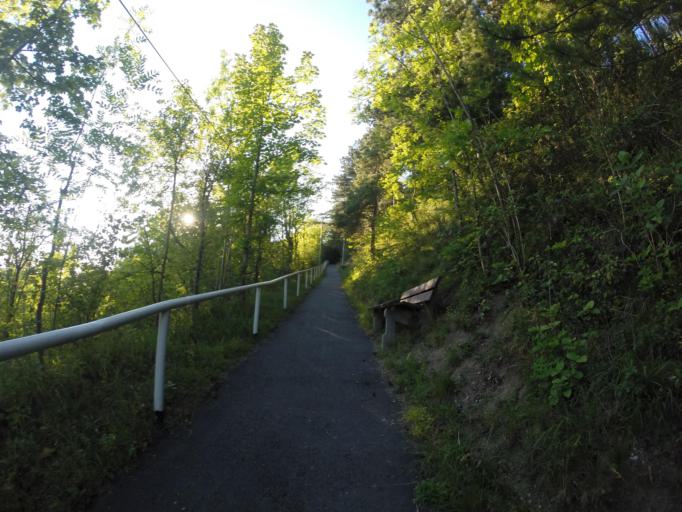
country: DE
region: Thuringia
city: Jena
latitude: 50.9230
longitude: 11.6243
